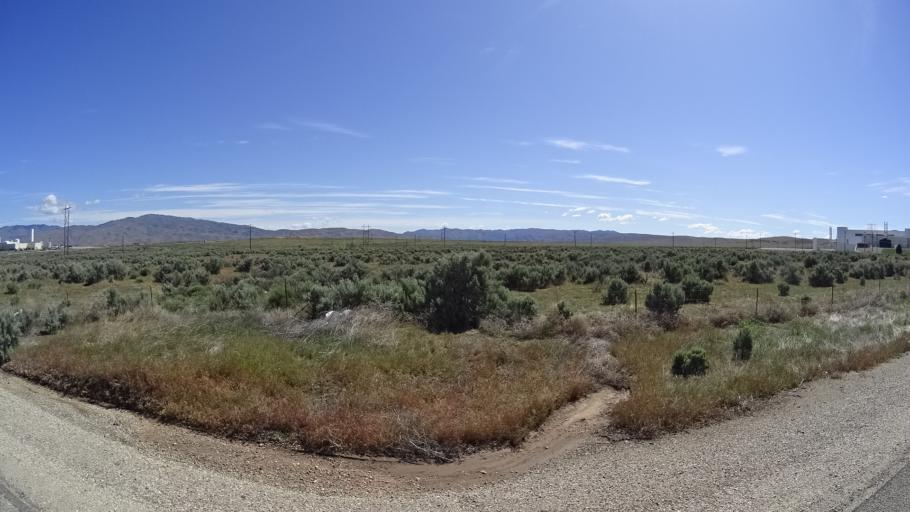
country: US
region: Idaho
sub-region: Ada County
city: Boise
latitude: 43.5144
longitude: -116.1439
